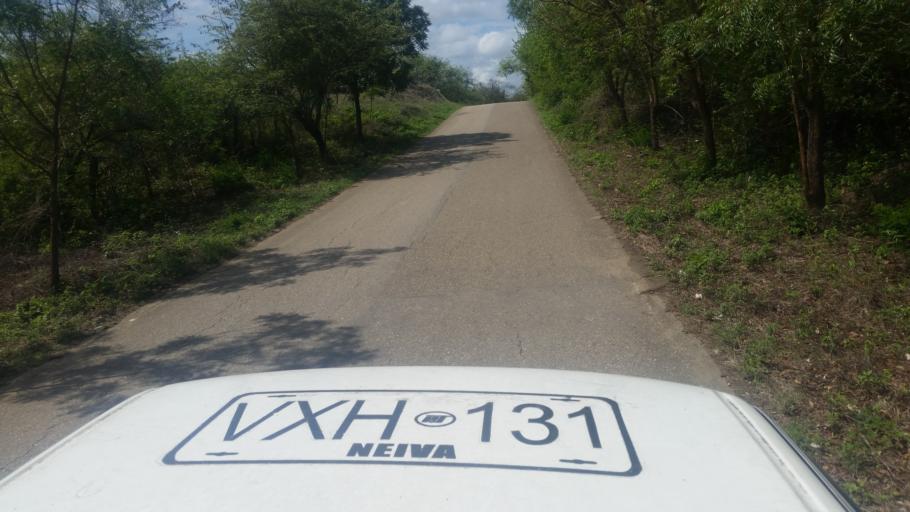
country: CO
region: Huila
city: Villavieja
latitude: 3.2001
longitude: -75.2104
